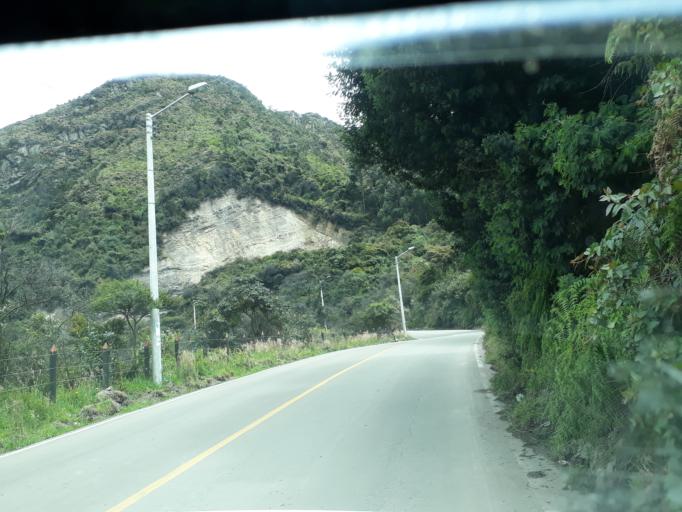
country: CO
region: Cundinamarca
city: Sutatausa
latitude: 5.1919
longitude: -73.8854
